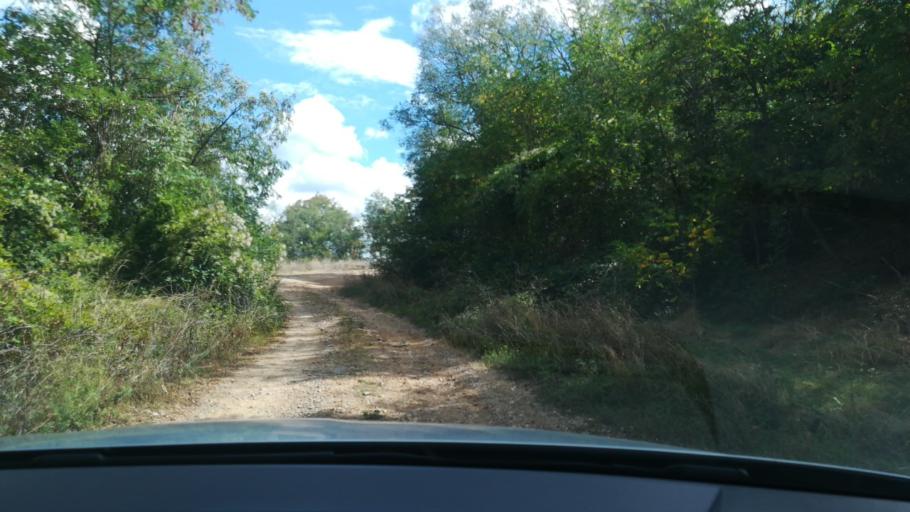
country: MK
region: Delcevo
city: Delcevo
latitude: 41.8939
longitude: 22.8049
